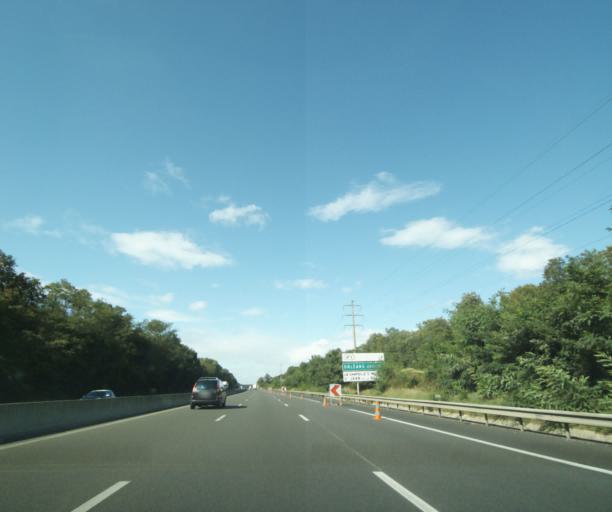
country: FR
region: Centre
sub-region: Departement du Loiret
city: Saint-Pryve-Saint-Mesmin
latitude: 47.8513
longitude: 1.8664
